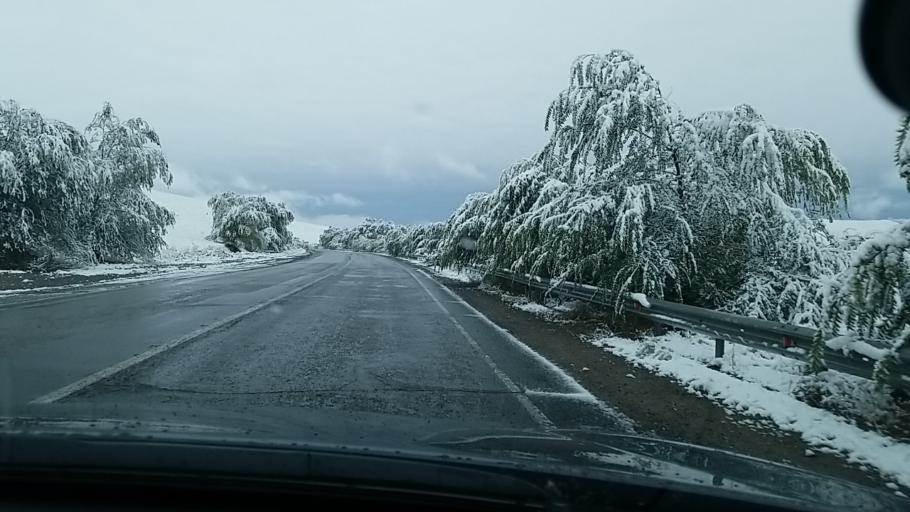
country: KZ
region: Almaty Oblysy
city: Burunday
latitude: 43.2902
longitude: 76.2460
